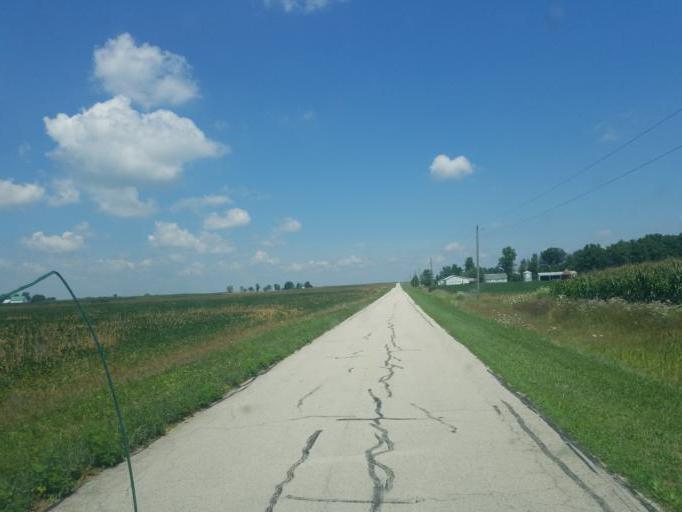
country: US
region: Ohio
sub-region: Allen County
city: Spencerville
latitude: 40.6697
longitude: -84.4350
